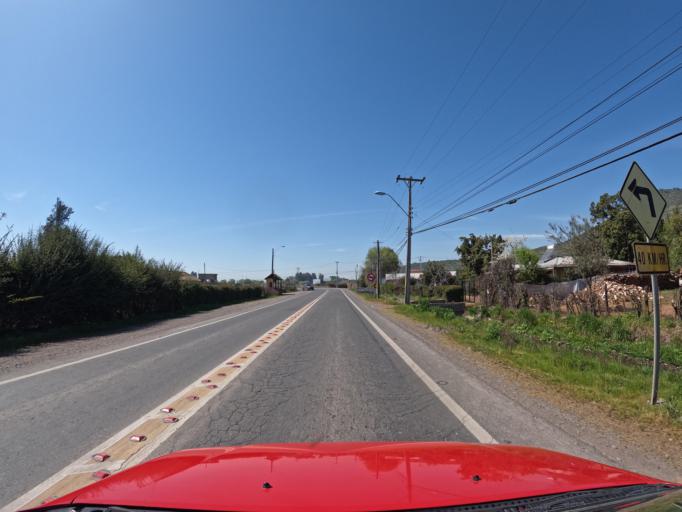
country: CL
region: Maule
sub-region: Provincia de Curico
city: Rauco
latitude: -35.0075
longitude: -71.4034
